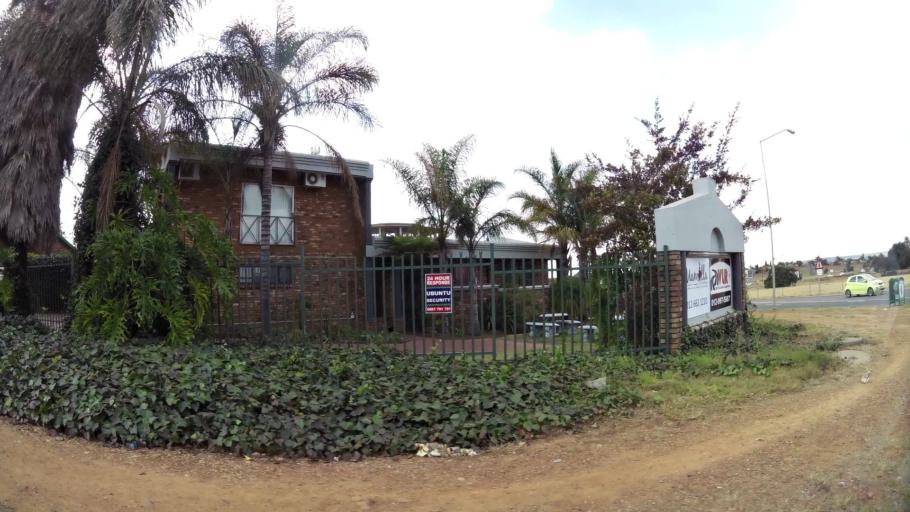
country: ZA
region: Gauteng
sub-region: City of Tshwane Metropolitan Municipality
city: Centurion
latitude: -25.8433
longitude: 28.2729
